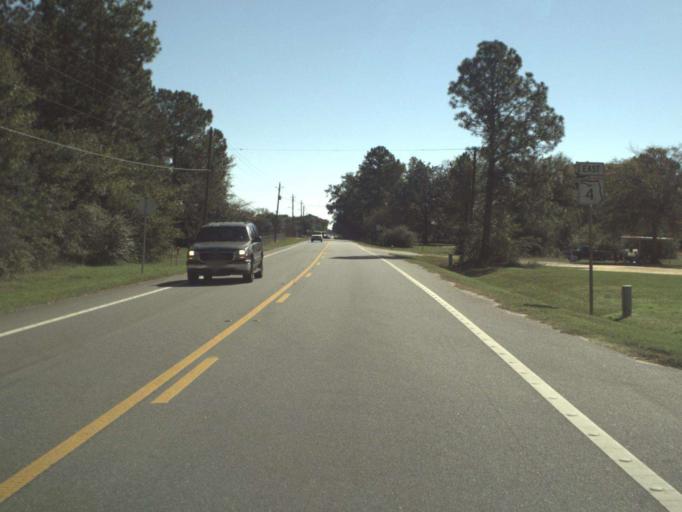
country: US
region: Florida
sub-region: Okaloosa County
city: Crestview
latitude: 30.7843
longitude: -86.6826
